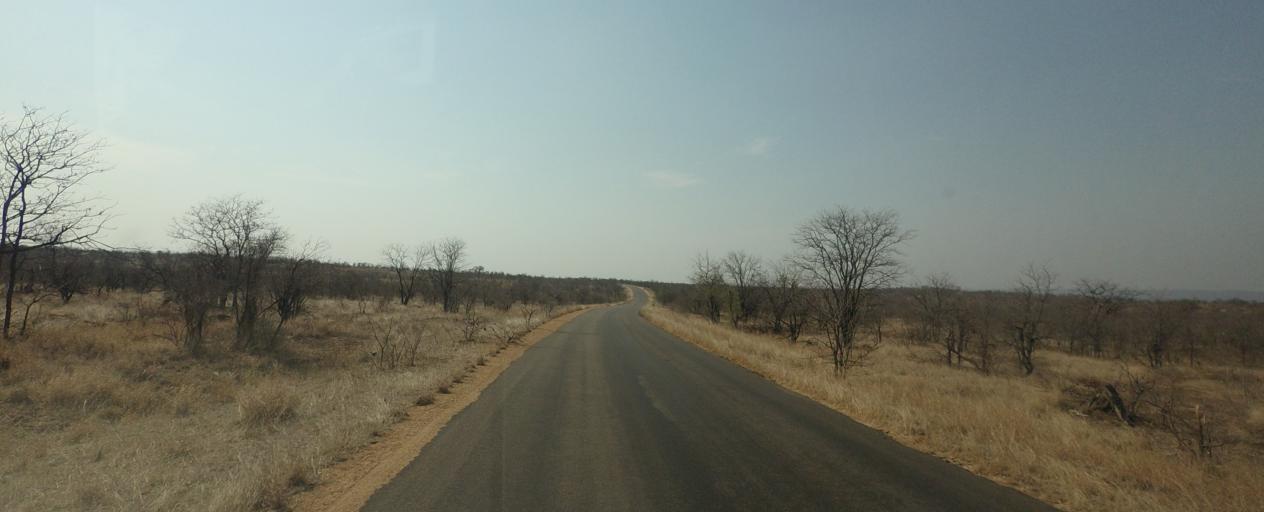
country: ZA
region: Limpopo
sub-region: Mopani District Municipality
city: Phalaborwa
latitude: -23.9467
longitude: 31.6151
